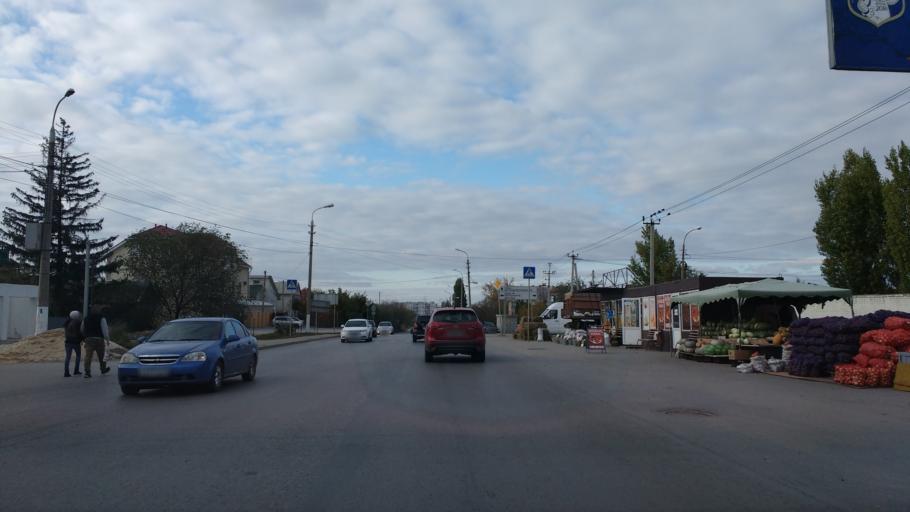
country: RU
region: Volgograd
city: Volgograd
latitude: 48.7671
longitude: 44.5285
